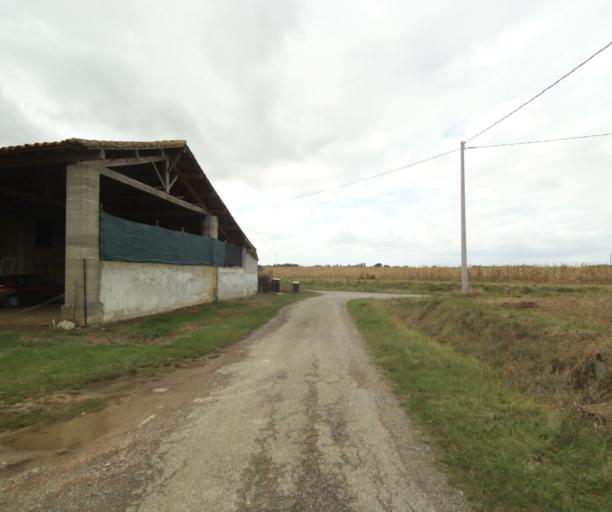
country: FR
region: Midi-Pyrenees
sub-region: Departement du Tarn-et-Garonne
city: Finhan
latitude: 43.8927
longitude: 1.1074
